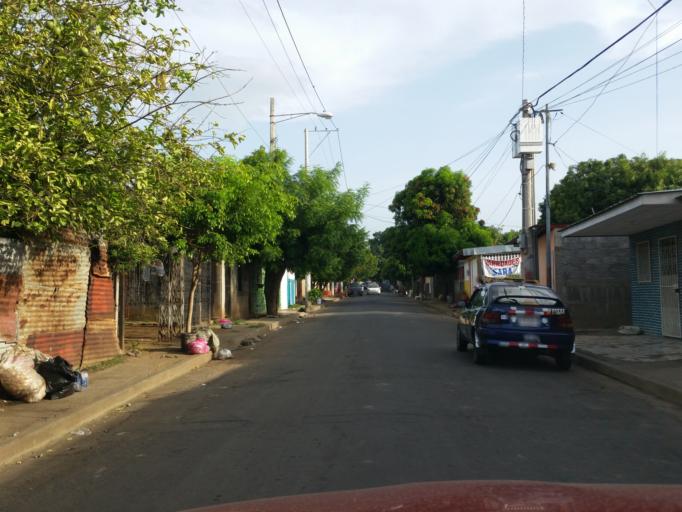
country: NI
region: Managua
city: Managua
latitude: 12.1488
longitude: -86.2801
